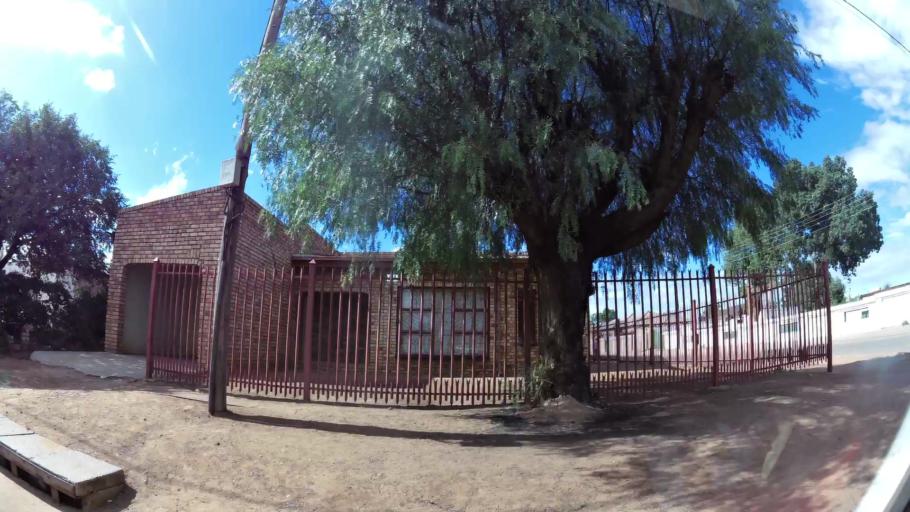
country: ZA
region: Limpopo
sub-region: Waterberg District Municipality
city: Bela-Bela
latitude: -24.8879
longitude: 28.3147
